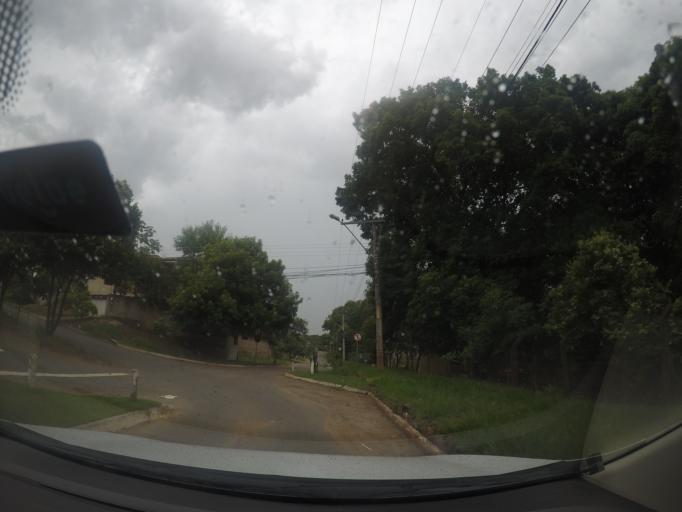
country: BR
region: Goias
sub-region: Goiania
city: Goiania
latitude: -16.6412
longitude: -49.2237
